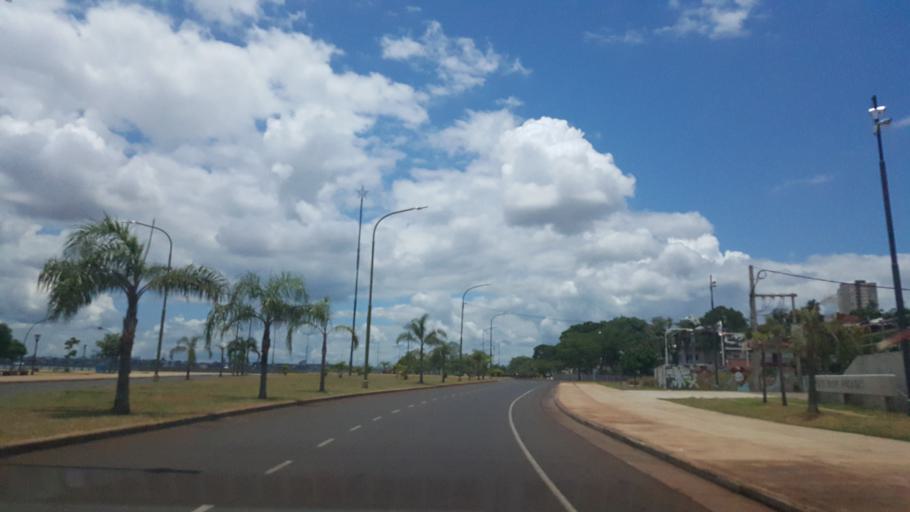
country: AR
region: Misiones
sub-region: Departamento de Capital
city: Posadas
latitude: -27.3523
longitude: -55.9009
